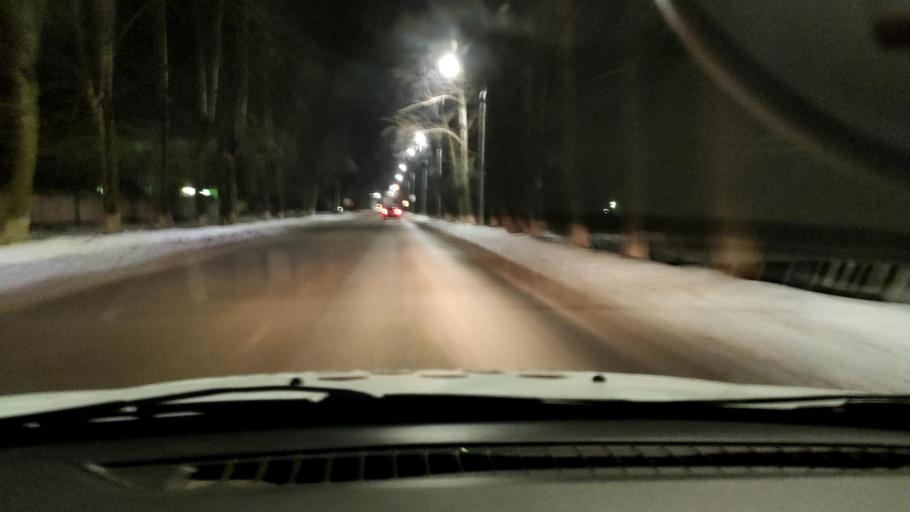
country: RU
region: Perm
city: Kultayevo
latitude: 57.9790
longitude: 55.9156
